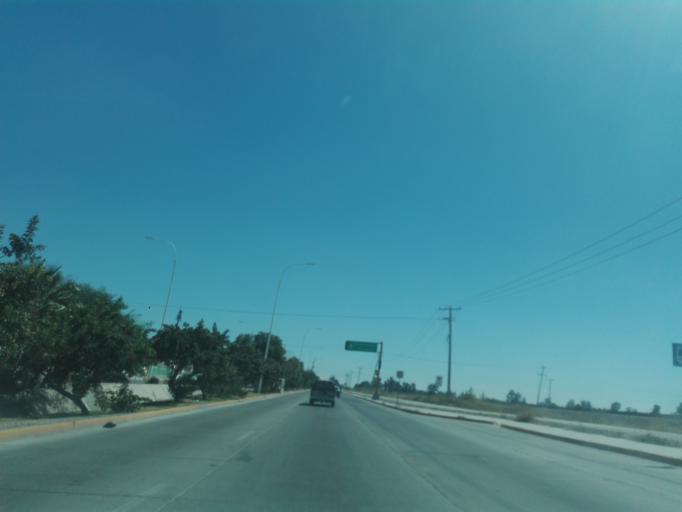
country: MX
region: Guanajuato
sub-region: Leon
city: San Jose de Duran (Los Troncoso)
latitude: 21.0790
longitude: -101.6568
